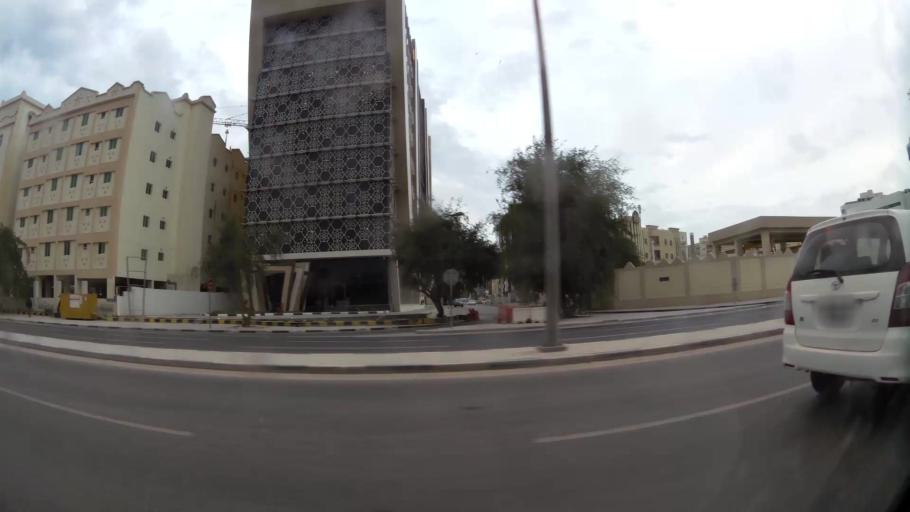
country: QA
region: Baladiyat ad Dawhah
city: Doha
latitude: 25.2667
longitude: 51.5259
